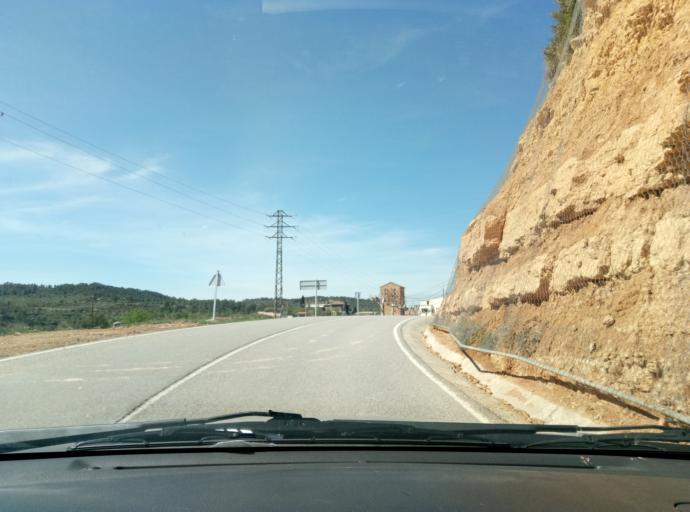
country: ES
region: Catalonia
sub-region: Provincia de Tarragona
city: Ulldemolins
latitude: 41.4237
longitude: 0.8650
